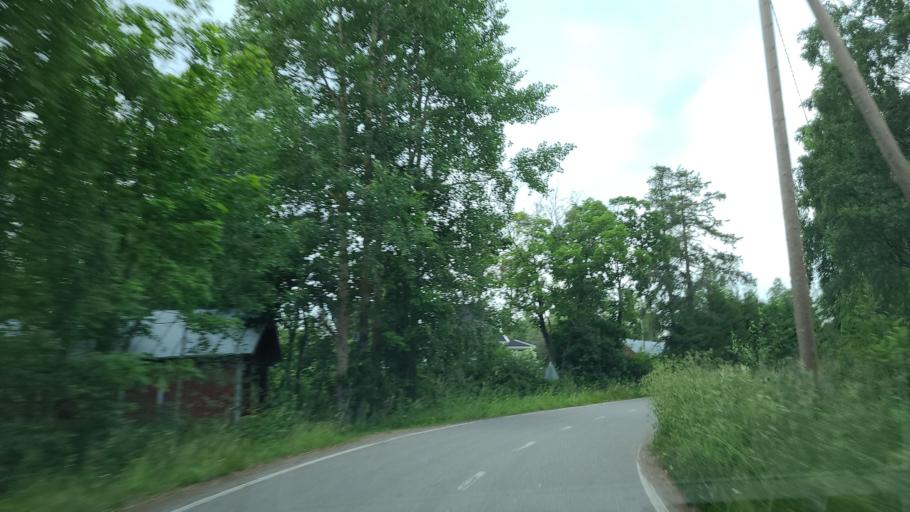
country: FI
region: Ostrobothnia
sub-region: Vaasa
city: Replot
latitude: 63.1657
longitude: 21.2554
